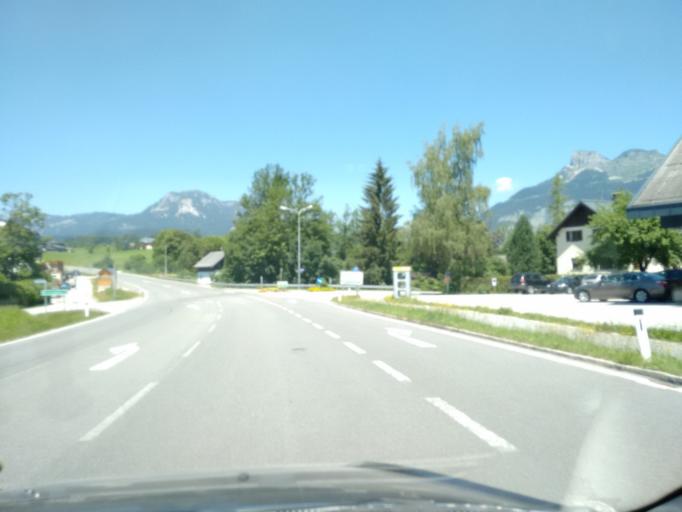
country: AT
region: Styria
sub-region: Politischer Bezirk Liezen
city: Bad Aussee
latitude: 47.6101
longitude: 13.7732
